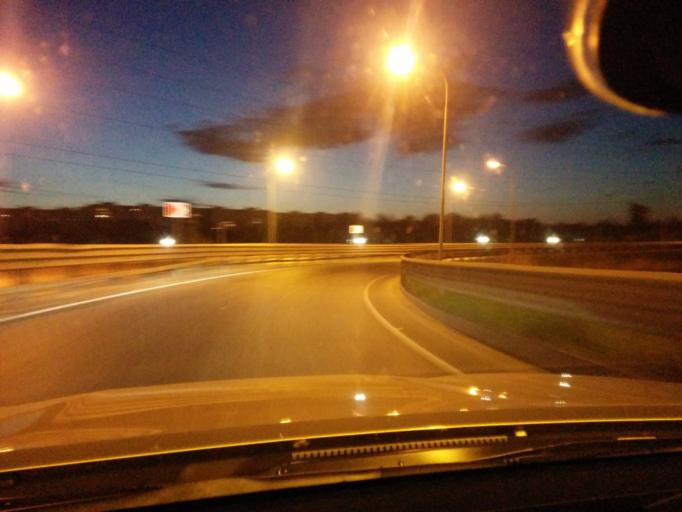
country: RU
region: St.-Petersburg
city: Obukhovo
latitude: 59.8253
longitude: 30.4299
